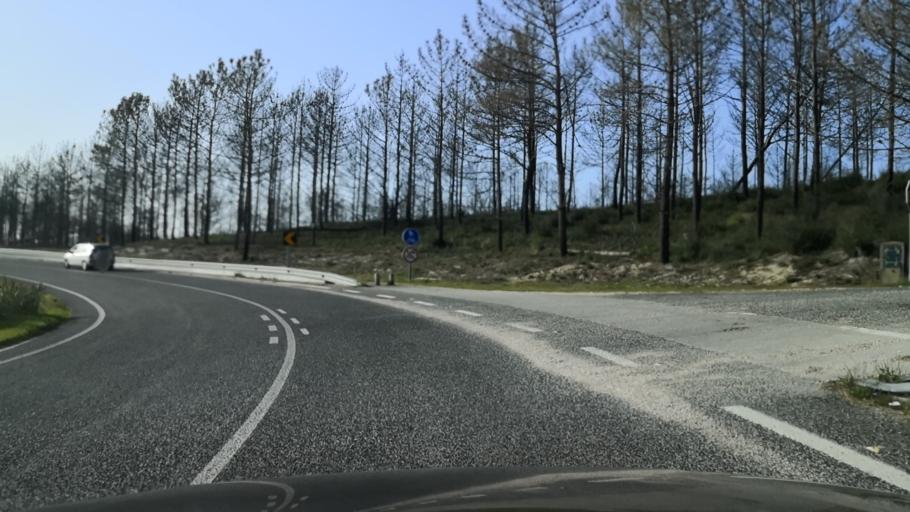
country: PT
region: Leiria
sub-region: Marinha Grande
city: Marinha Grande
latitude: 39.7467
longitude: -8.9933
